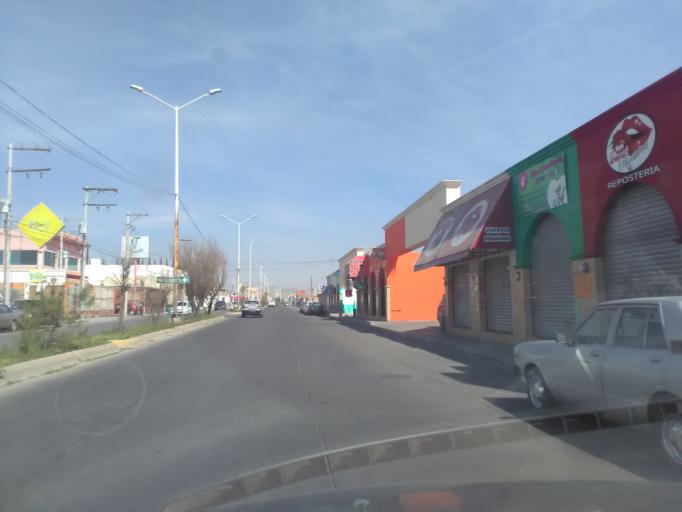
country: MX
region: Durango
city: Victoria de Durango
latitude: 24.0539
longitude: -104.6277
